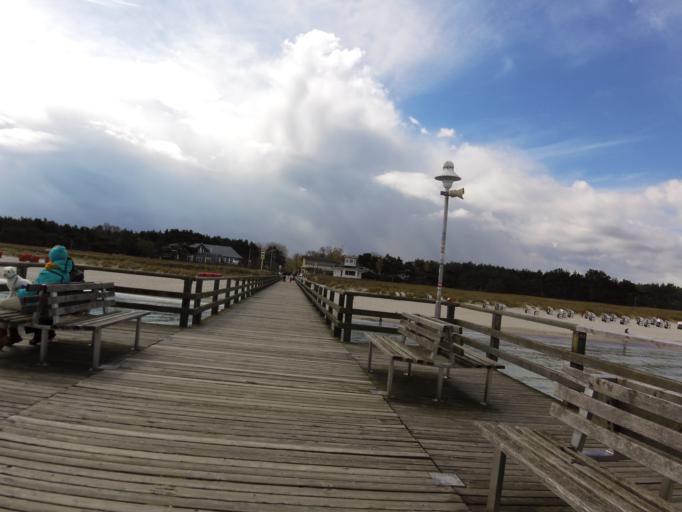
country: DE
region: Mecklenburg-Vorpommern
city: Ostseebad Prerow
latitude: 54.4541
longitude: 12.5703
